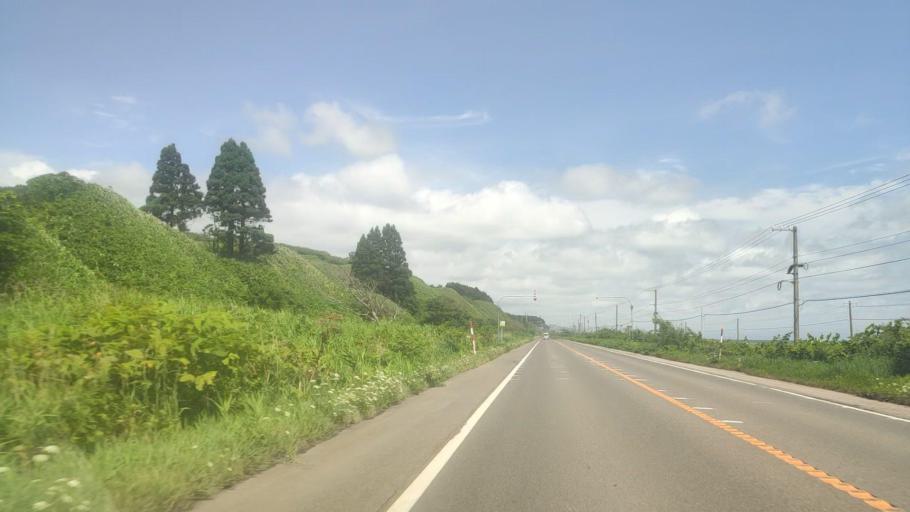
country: JP
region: Hokkaido
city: Niseko Town
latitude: 42.3449
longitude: 140.2819
